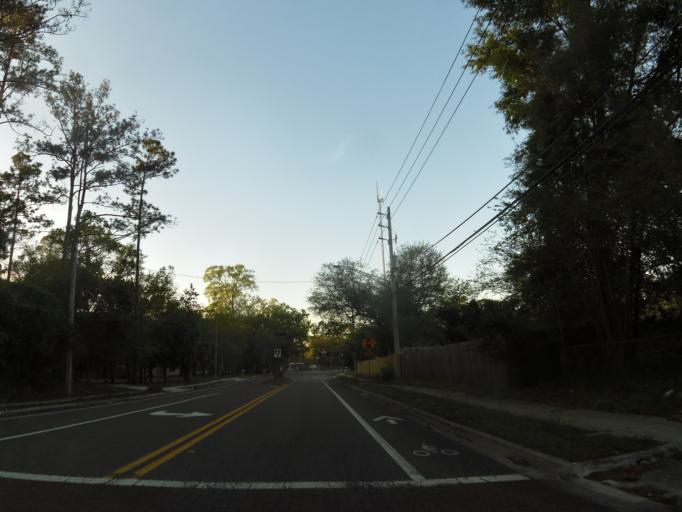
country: US
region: Florida
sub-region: Duval County
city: Jacksonville
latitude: 30.2741
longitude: -81.5711
